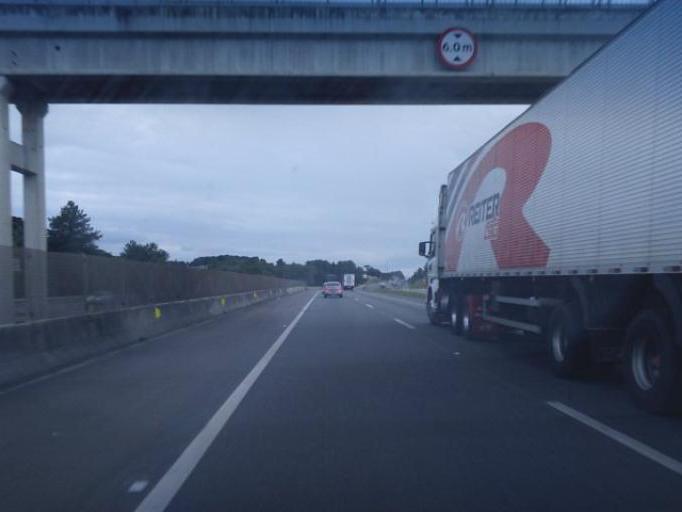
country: BR
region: Parana
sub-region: Sao Jose Dos Pinhais
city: Sao Jose dos Pinhais
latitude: -25.6994
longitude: -49.1437
